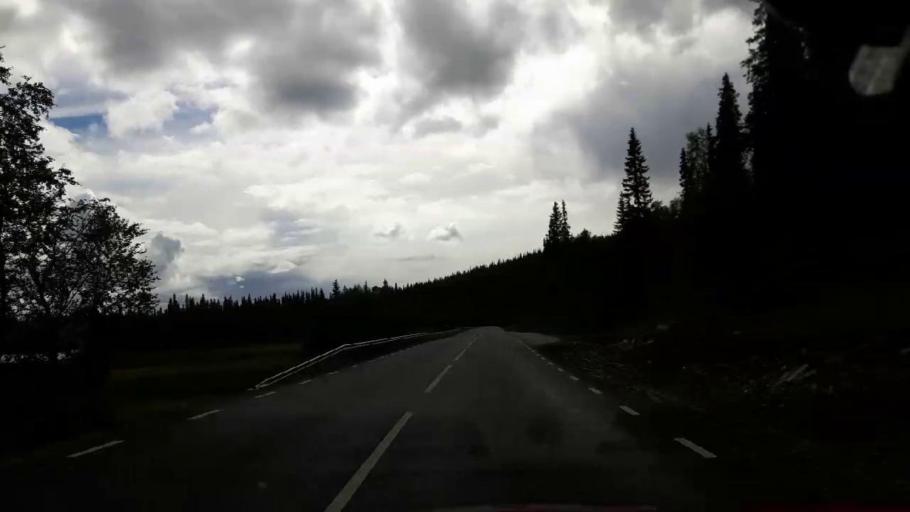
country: NO
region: Nord-Trondelag
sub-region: Royrvik
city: Royrvik
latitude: 64.8172
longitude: 14.0621
